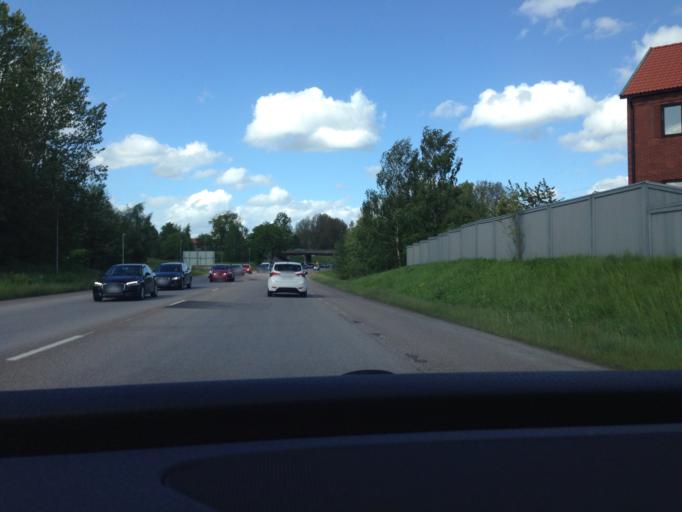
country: SE
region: Vaestra Goetaland
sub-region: Skovde Kommun
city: Skoevde
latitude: 58.3966
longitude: 13.8402
